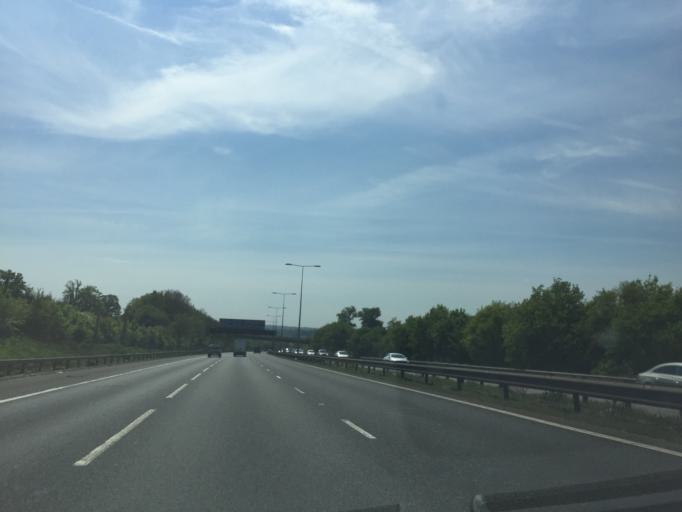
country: GB
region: England
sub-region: Essex
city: Epping
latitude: 51.6961
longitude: 0.1400
